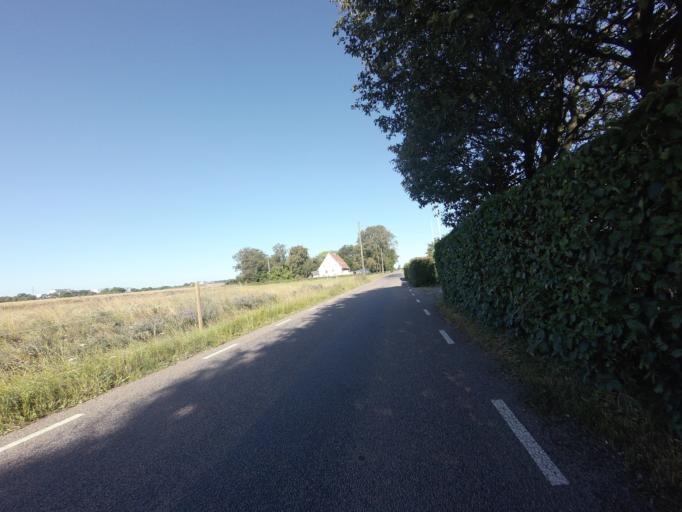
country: SE
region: Skane
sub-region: Hoganas Kommun
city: Hoganas
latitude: 56.1653
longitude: 12.5945
